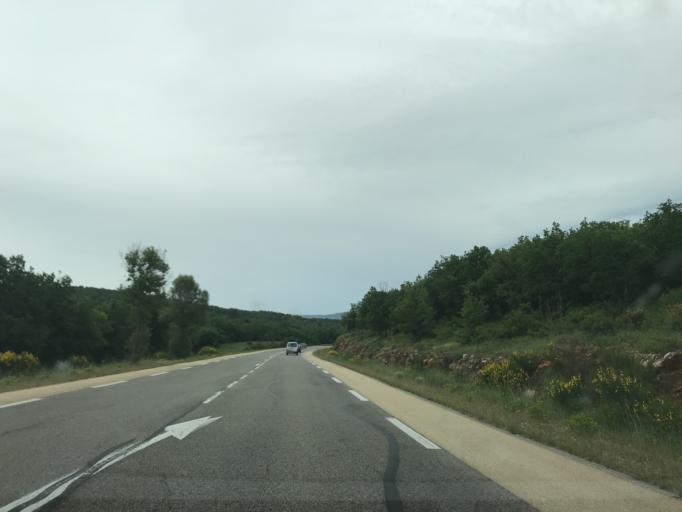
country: FR
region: Provence-Alpes-Cote d'Azur
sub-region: Departement du Var
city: Pourrieres
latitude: 43.5357
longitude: 5.8116
